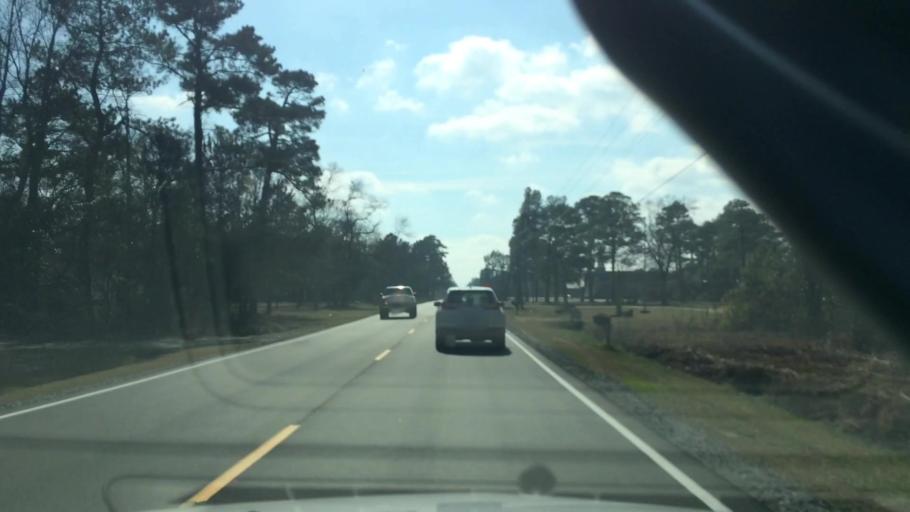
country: US
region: North Carolina
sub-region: Duplin County
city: Beulaville
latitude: 34.9774
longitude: -77.7606
